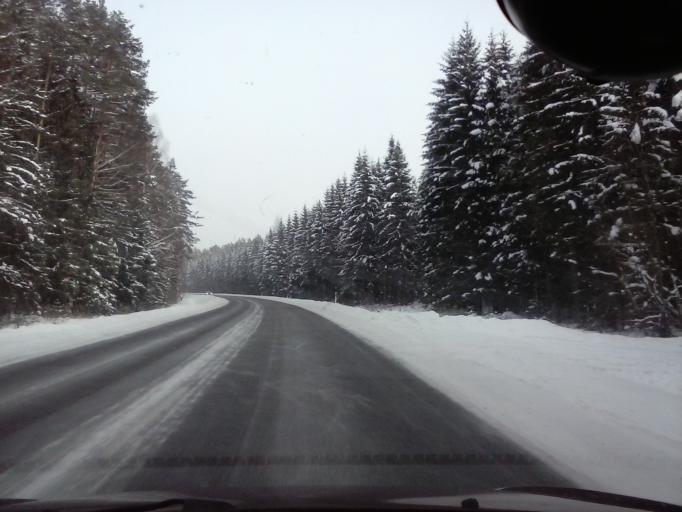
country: EE
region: Paernumaa
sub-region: Saarde vald
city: Kilingi-Nomme
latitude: 58.2211
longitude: 25.0973
